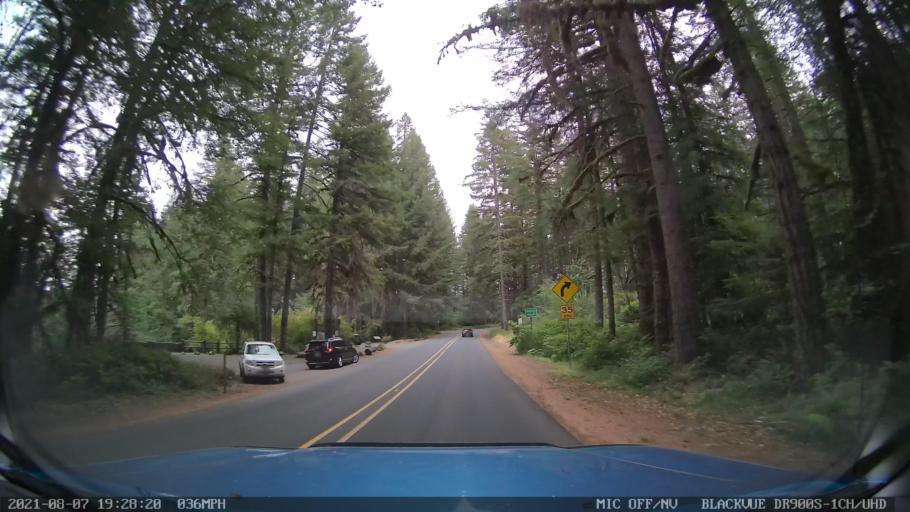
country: US
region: Oregon
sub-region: Linn County
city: Lyons
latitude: 44.8841
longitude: -122.6405
